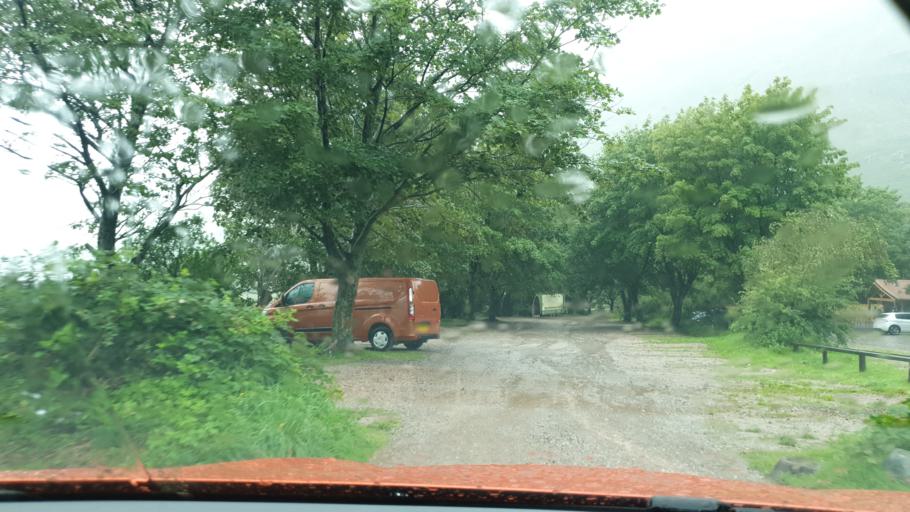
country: GB
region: England
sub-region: Cumbria
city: Keswick
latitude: 54.4557
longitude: -3.2619
